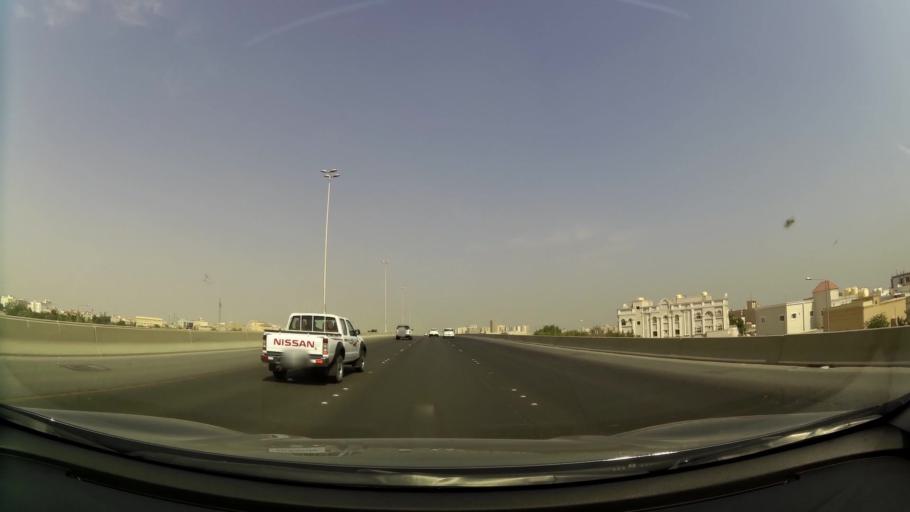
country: KW
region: Al Ahmadi
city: Al Fahahil
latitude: 29.0888
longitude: 48.1157
